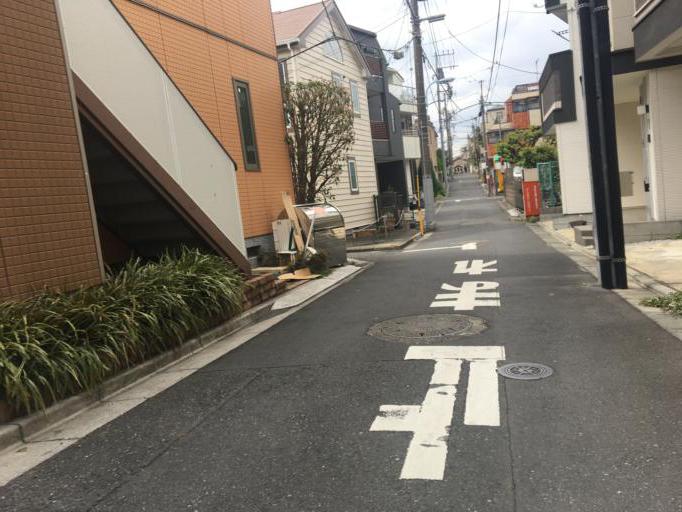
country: JP
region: Tokyo
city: Tokyo
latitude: 35.7040
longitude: 139.6577
